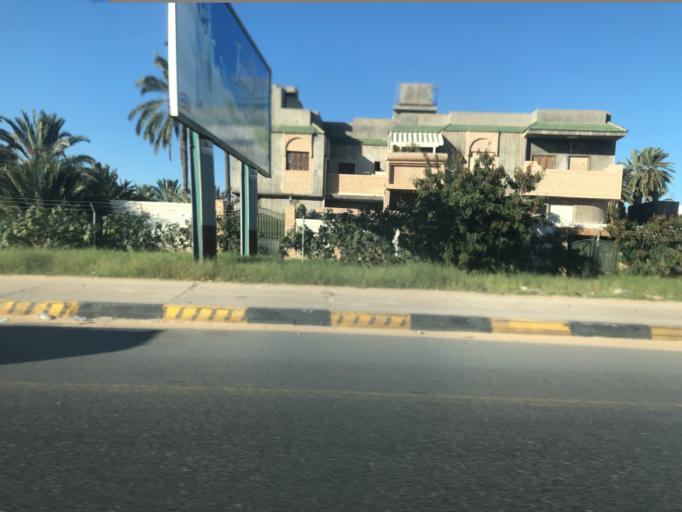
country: LY
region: Tripoli
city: Tripoli
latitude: 32.8694
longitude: 13.2595
